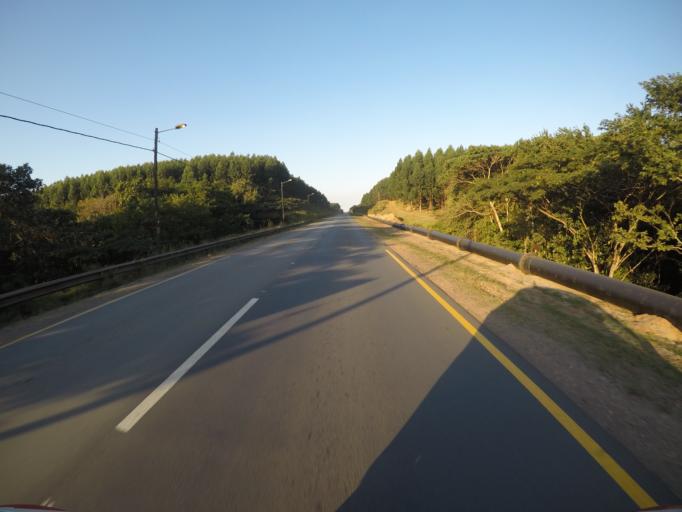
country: ZA
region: KwaZulu-Natal
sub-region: uThungulu District Municipality
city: KwaMbonambi
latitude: -28.6833
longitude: 32.1496
